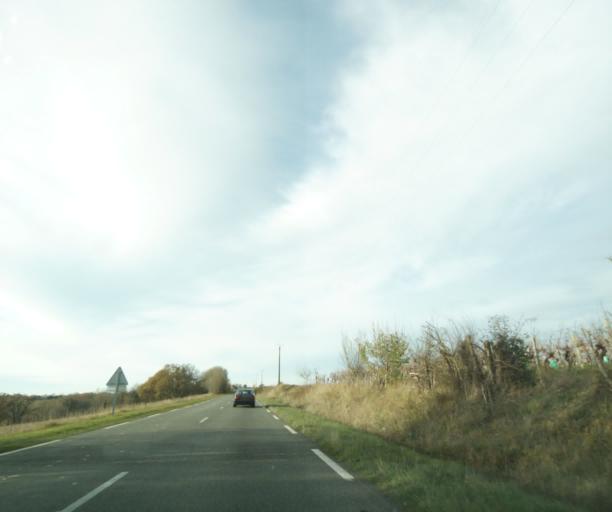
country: FR
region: Midi-Pyrenees
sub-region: Departement du Gers
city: Eauze
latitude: 43.7834
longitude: 0.1139
